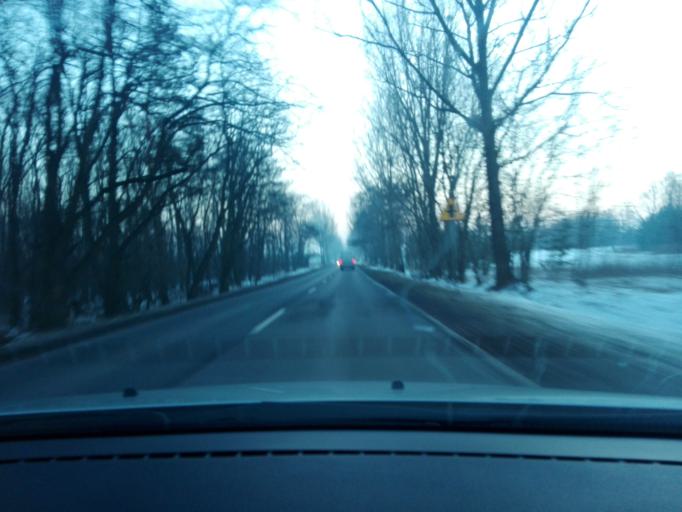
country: PL
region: Lodz Voivodeship
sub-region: Powiat zgierski
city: Zgierz
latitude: 51.9050
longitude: 19.4289
